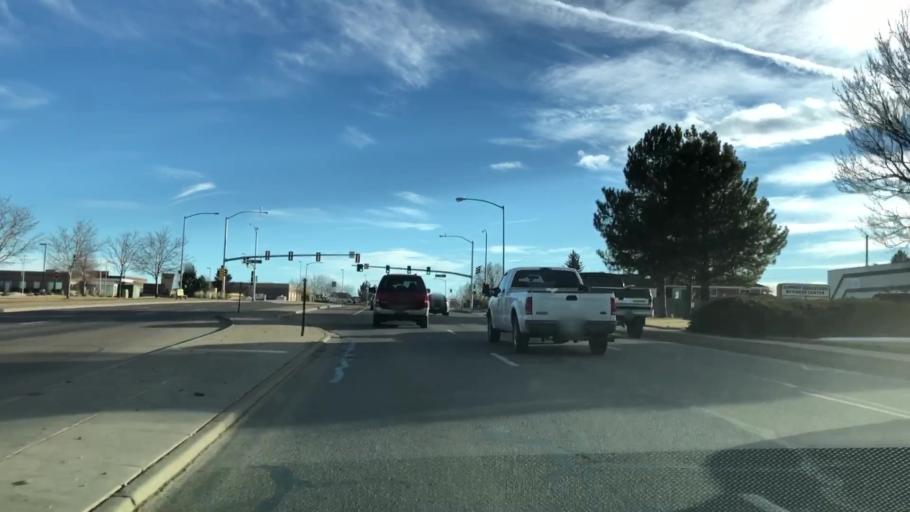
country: US
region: Colorado
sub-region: Adams County
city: Aurora
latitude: 39.7205
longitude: -104.7915
